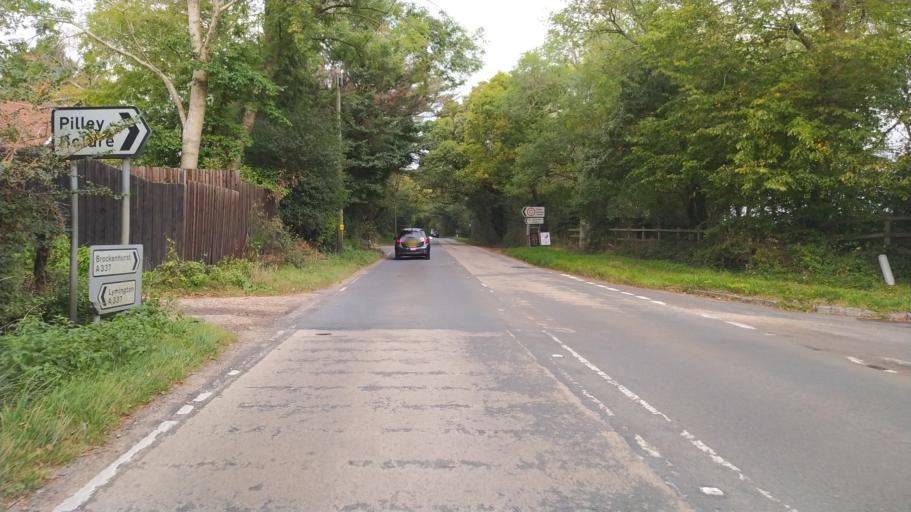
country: GB
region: England
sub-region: Hampshire
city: Lymington
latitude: 50.7829
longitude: -1.5601
